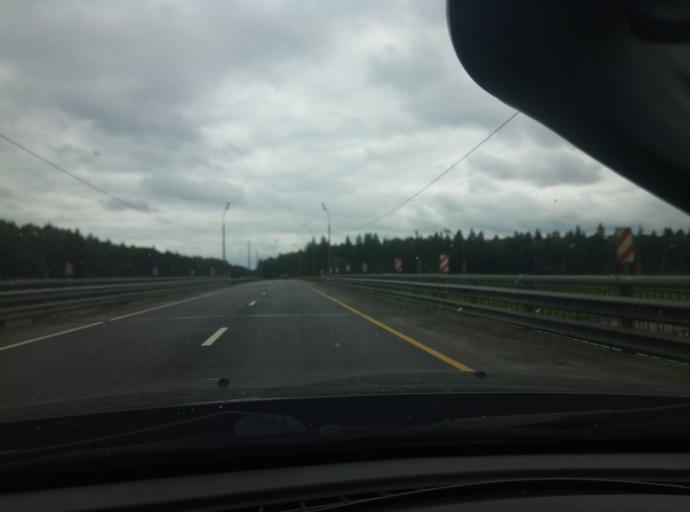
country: RU
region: Kaluga
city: Maloyaroslavets
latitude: 54.9790
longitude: 36.4916
